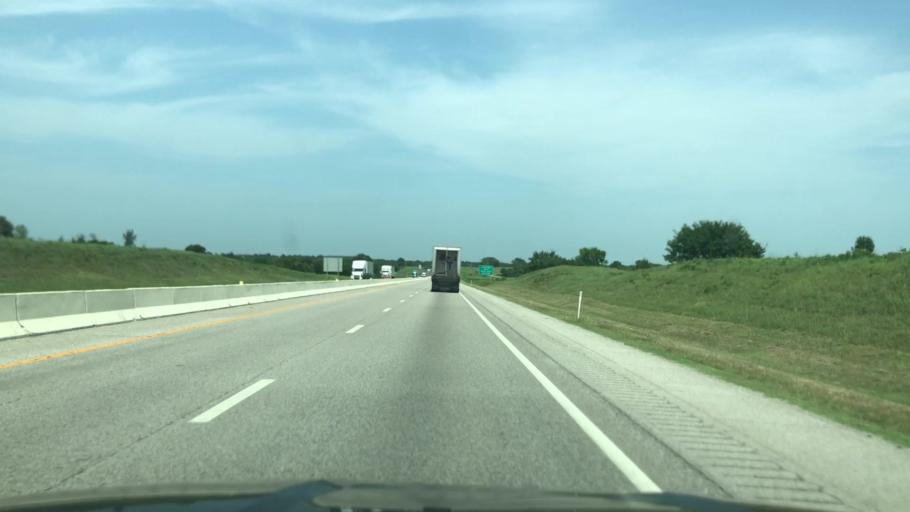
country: US
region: Oklahoma
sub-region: Craig County
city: Vinita
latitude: 36.6461
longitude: -95.1147
